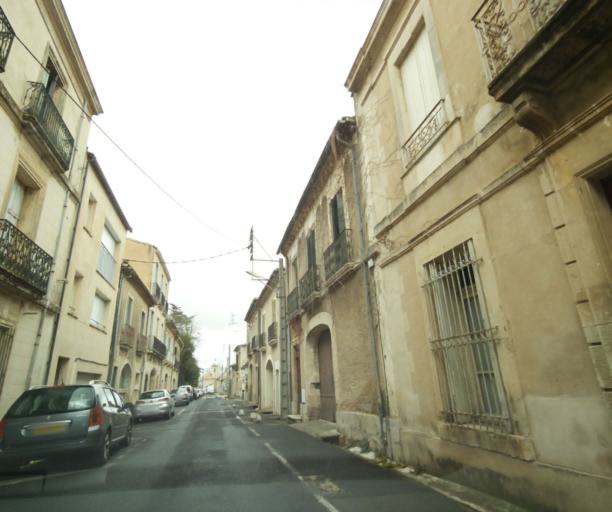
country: FR
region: Languedoc-Roussillon
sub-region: Departement de l'Herault
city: Cournonterral
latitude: 43.5557
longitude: 3.7147
